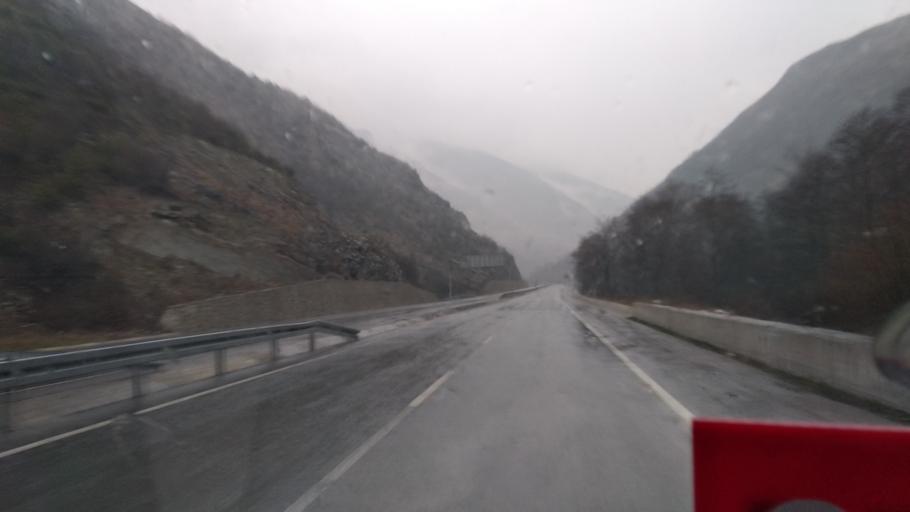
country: TR
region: Trabzon
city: Macka
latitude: 40.7912
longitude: 39.5809
